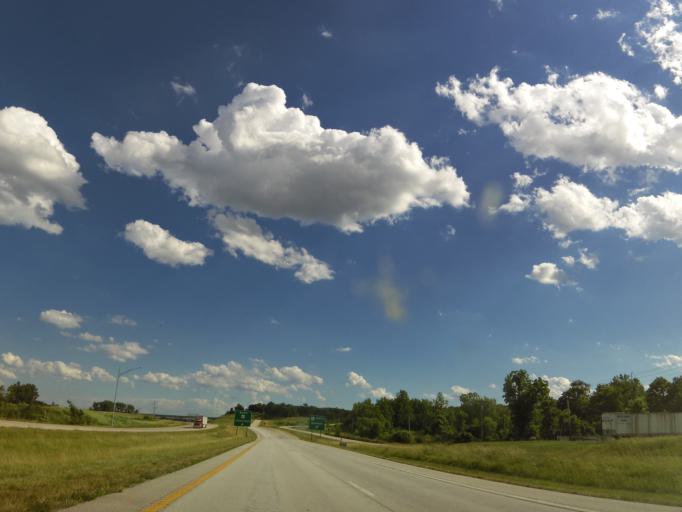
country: US
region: Missouri
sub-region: Clark County
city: Kahoka
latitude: 40.3685
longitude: -91.5886
